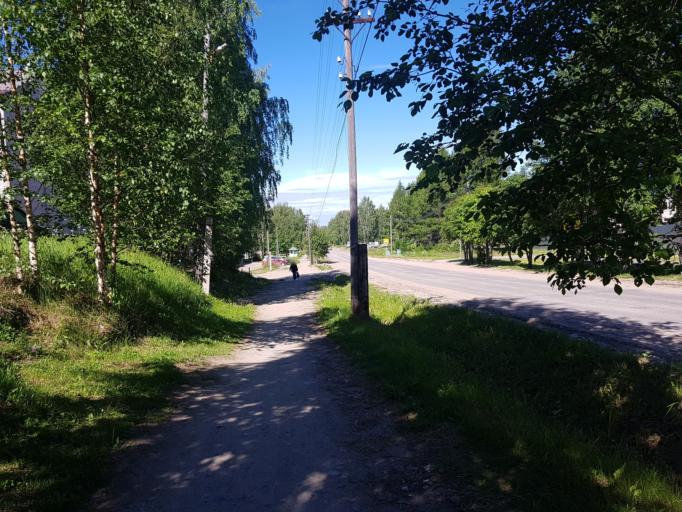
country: RU
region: Republic of Karelia
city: Kalevala
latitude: 65.1961
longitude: 31.2033
